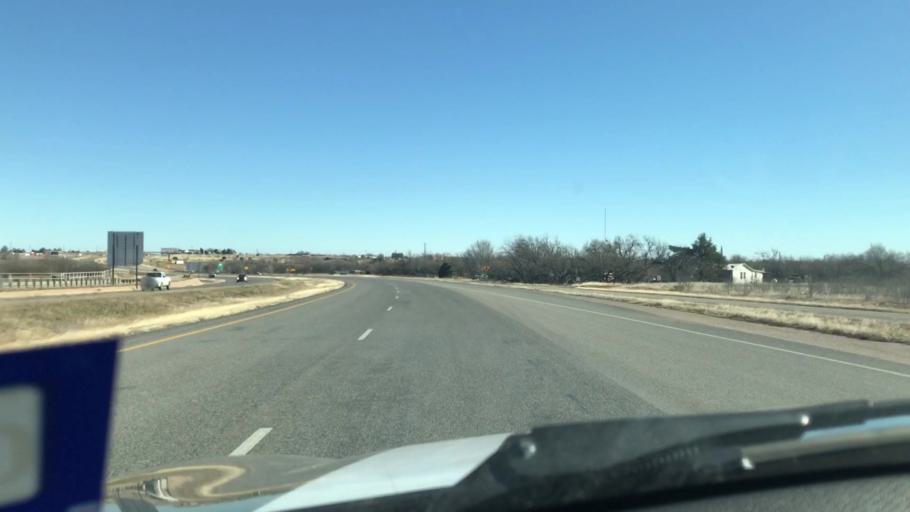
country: US
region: Texas
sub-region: Scurry County
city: Snyder
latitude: 32.7359
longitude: -100.9143
